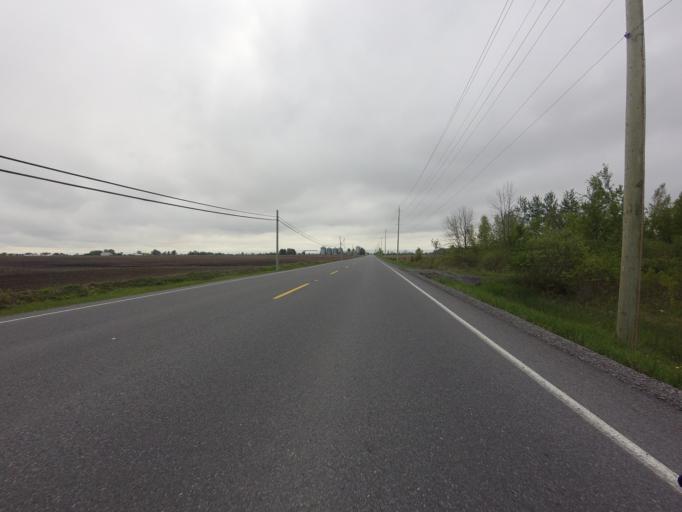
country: CA
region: Ontario
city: Casselman
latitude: 45.1281
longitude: -75.2449
